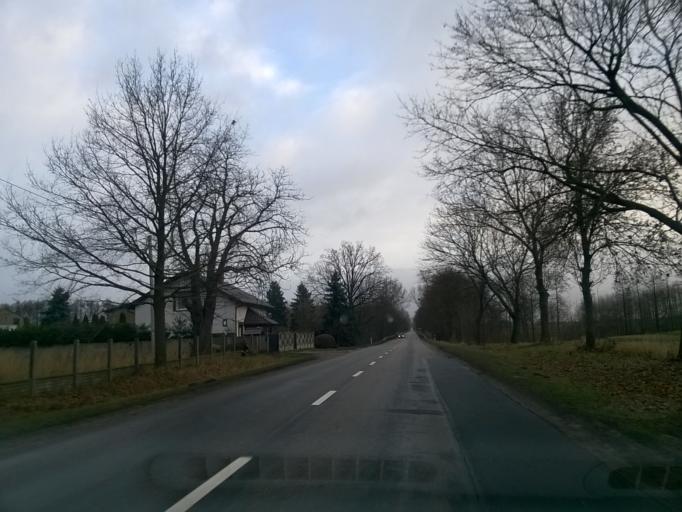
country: PL
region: Greater Poland Voivodeship
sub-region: Powiat wagrowiecki
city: Wagrowiec
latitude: 52.8556
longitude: 17.2722
